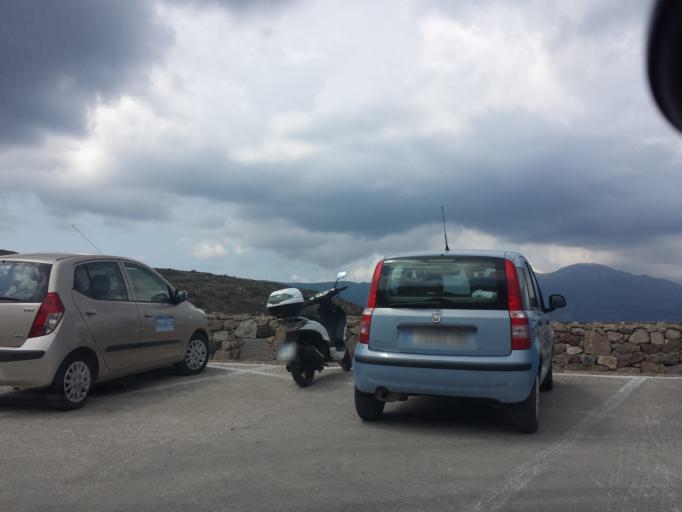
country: GR
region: South Aegean
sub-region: Nomos Kykladon
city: Milos
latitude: 36.7379
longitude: 24.4236
